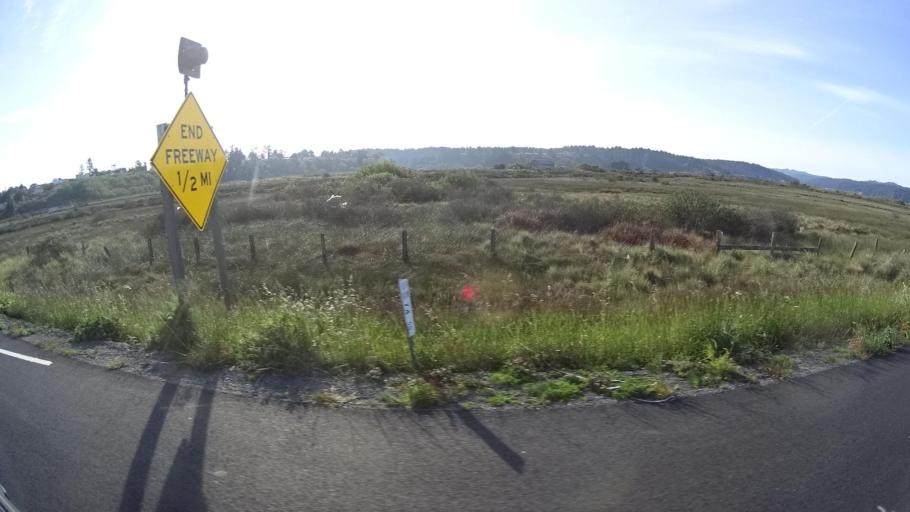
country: US
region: California
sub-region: Humboldt County
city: Bayview
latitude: 40.7543
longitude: -124.1920
